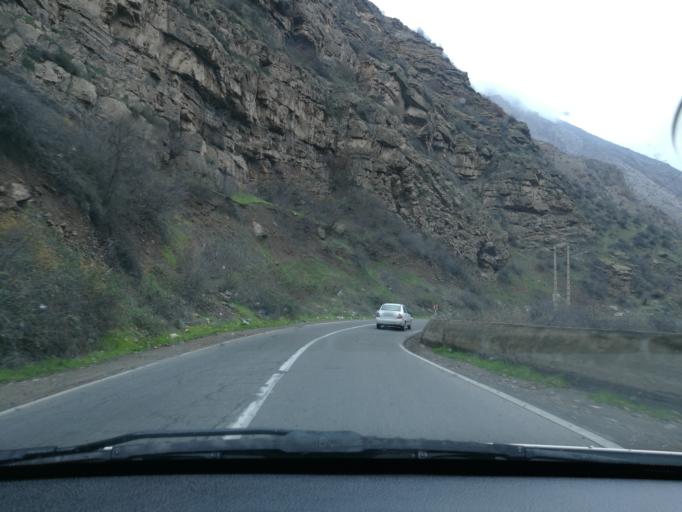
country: IR
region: Mazandaran
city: Chalus
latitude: 36.3070
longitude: 51.2474
